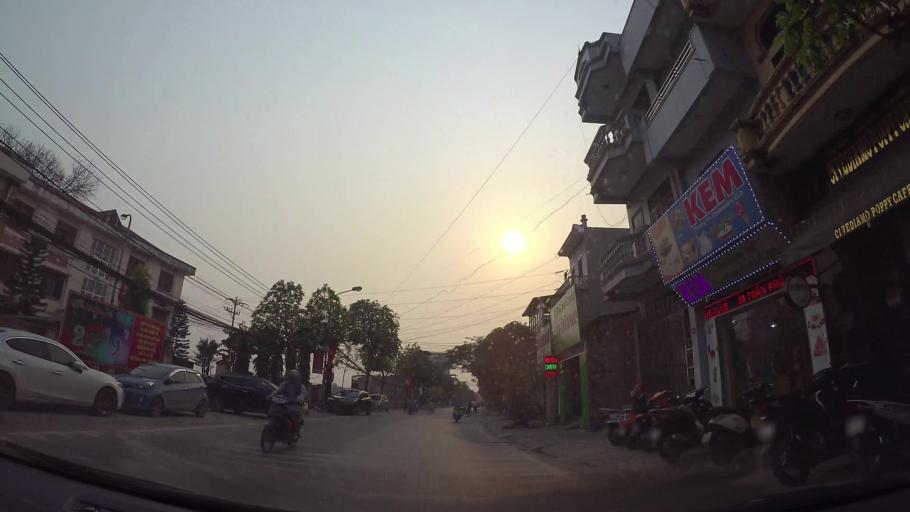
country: VN
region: Ha Noi
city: Thuong Tin
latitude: 20.8677
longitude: 105.8607
